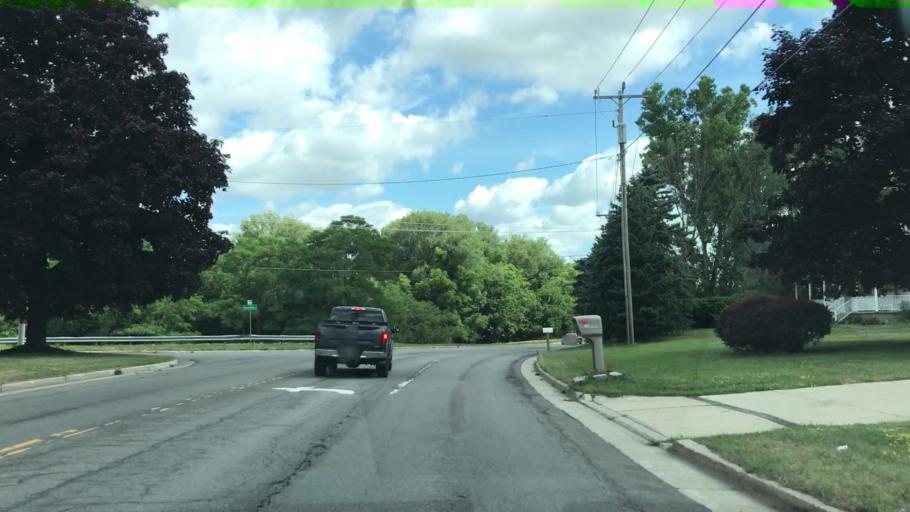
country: US
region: New York
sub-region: Erie County
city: Depew
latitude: 42.8976
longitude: -78.7085
